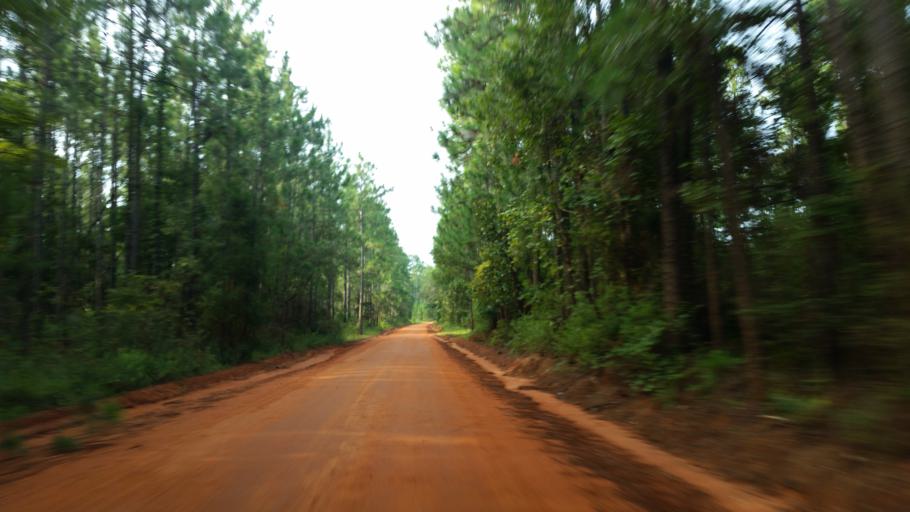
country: US
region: Alabama
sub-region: Escambia County
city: Atmore
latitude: 30.8865
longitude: -87.5826
